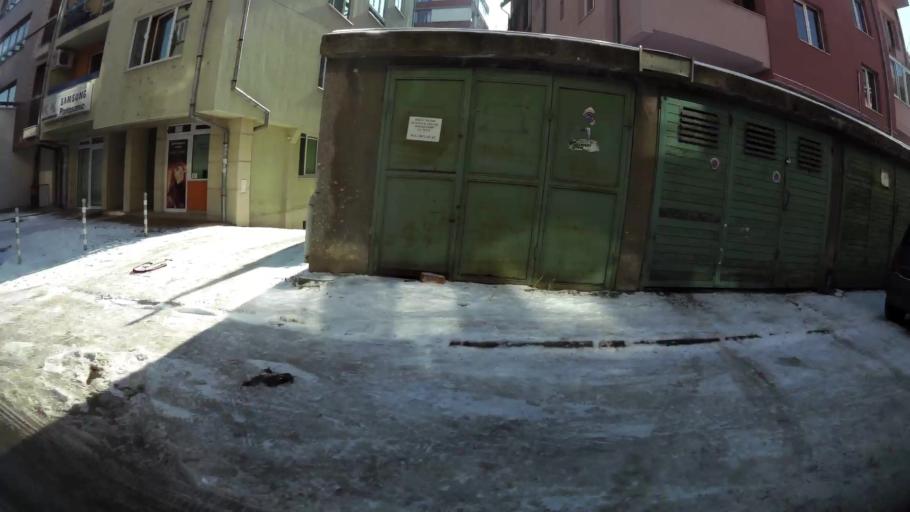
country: BG
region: Sofia-Capital
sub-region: Stolichna Obshtina
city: Sofia
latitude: 42.6748
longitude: 23.3204
